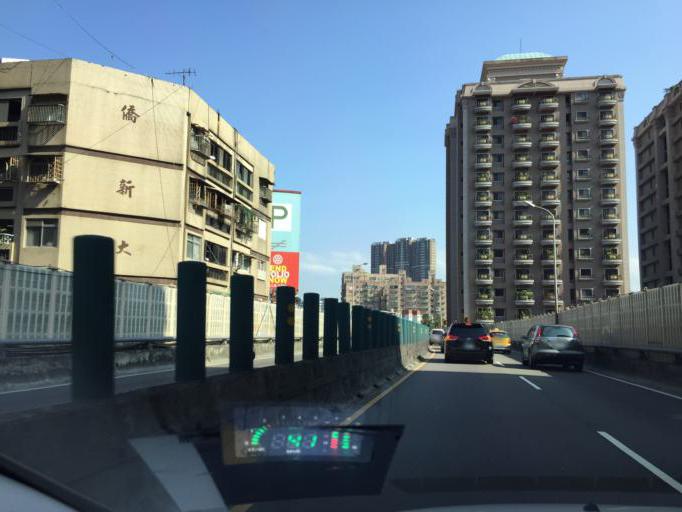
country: TW
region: Taipei
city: Taipei
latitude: 25.0590
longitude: 121.4888
